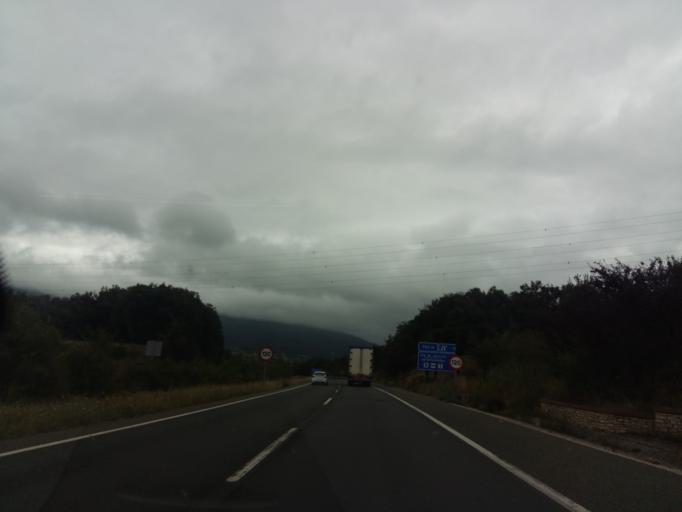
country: ES
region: Navarre
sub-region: Provincia de Navarra
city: Arbizu
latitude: 42.9063
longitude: -2.0466
